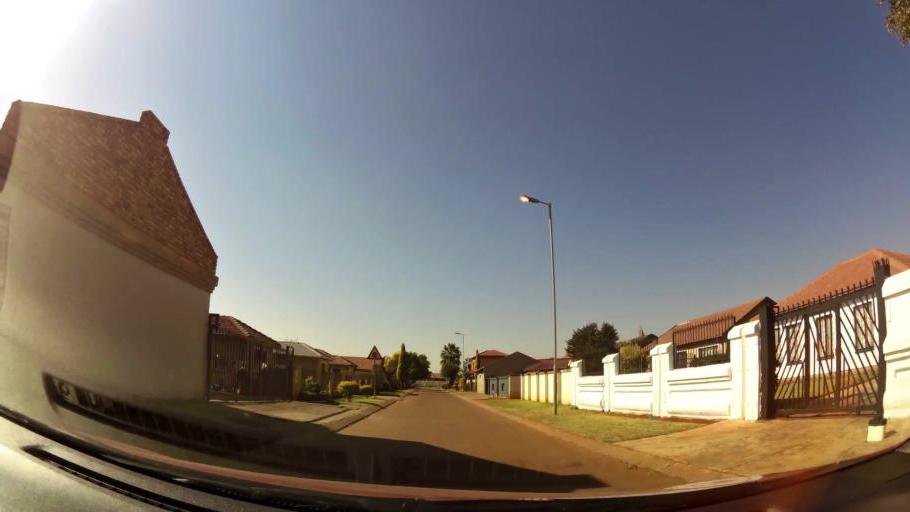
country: ZA
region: North-West
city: Ga-Rankuwa
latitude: -25.6357
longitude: 28.0811
